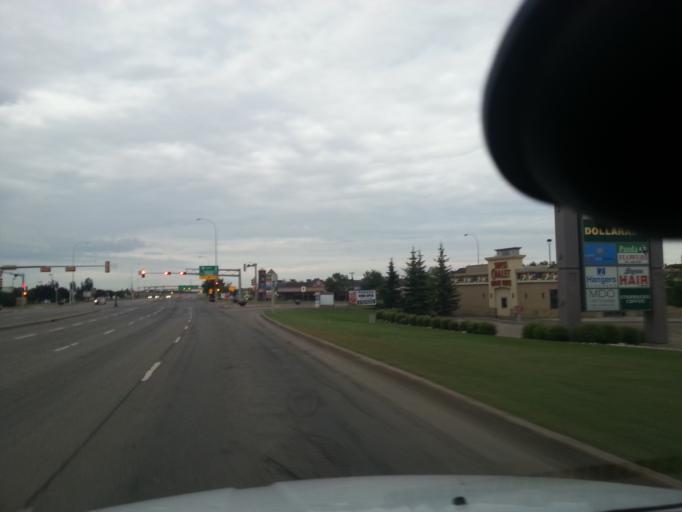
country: CA
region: Alberta
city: St. Albert
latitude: 53.6220
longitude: -113.6110
